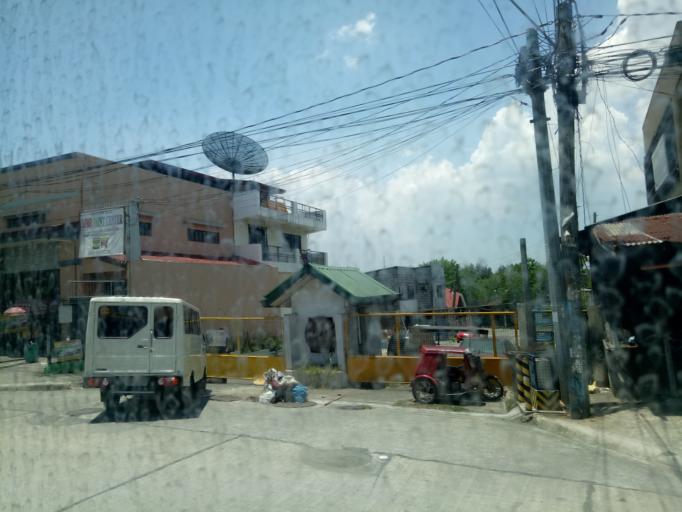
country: PH
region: Calabarzon
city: Bagong Pagasa
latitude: 14.7230
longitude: 121.0505
